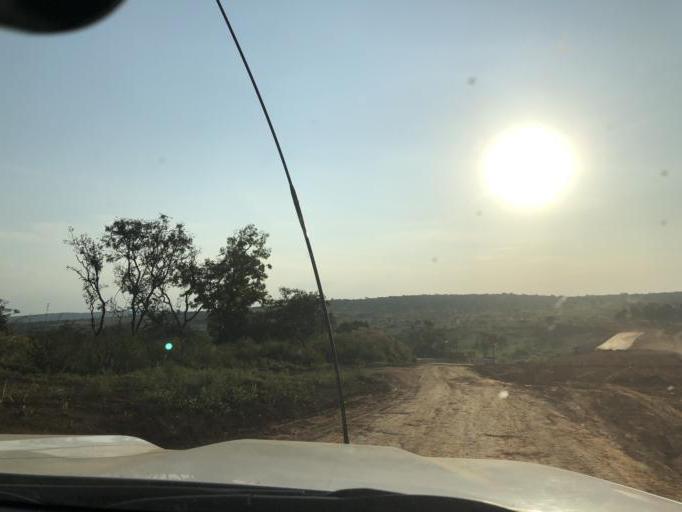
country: CF
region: Nana-Mambere
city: Bouar
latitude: 5.8949
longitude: 15.7622
